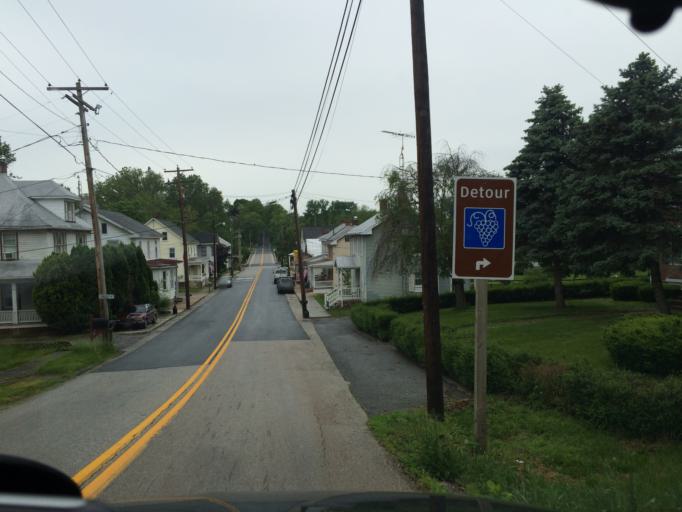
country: US
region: Maryland
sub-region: Frederick County
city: Woodsboro
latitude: 39.6041
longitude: -77.2673
